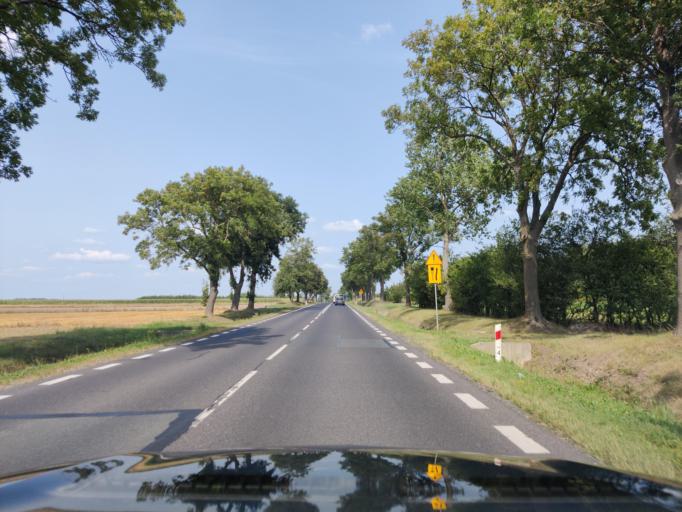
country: PL
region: Masovian Voivodeship
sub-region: Powiat pultuski
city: Pultusk
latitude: 52.7486
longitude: 21.1017
